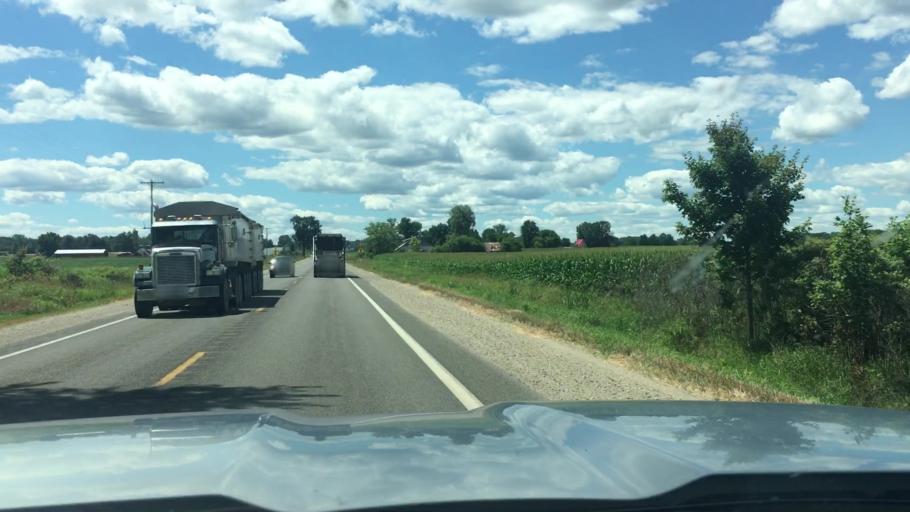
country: US
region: Michigan
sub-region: Montcalm County
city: Stanton
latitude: 43.1782
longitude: -85.0645
